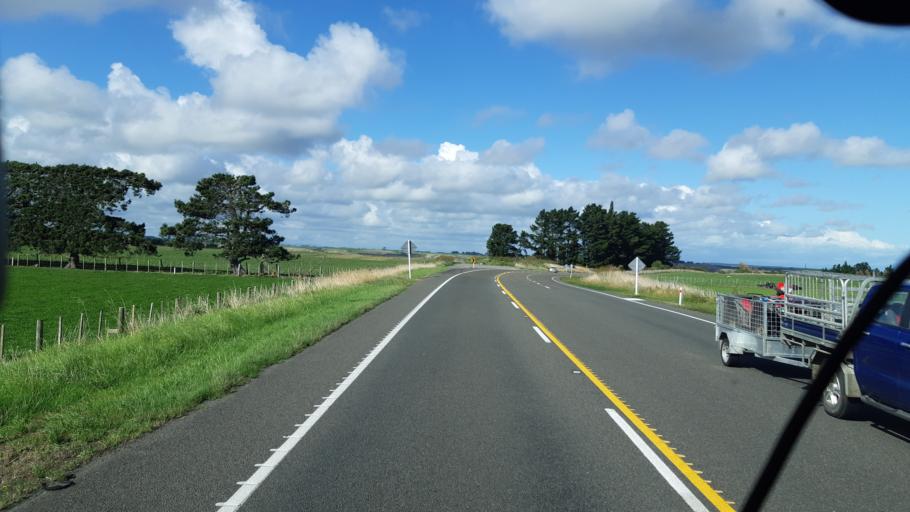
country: NZ
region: Manawatu-Wanganui
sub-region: Wanganui District
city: Wanganui
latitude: -39.9923
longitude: 175.1662
